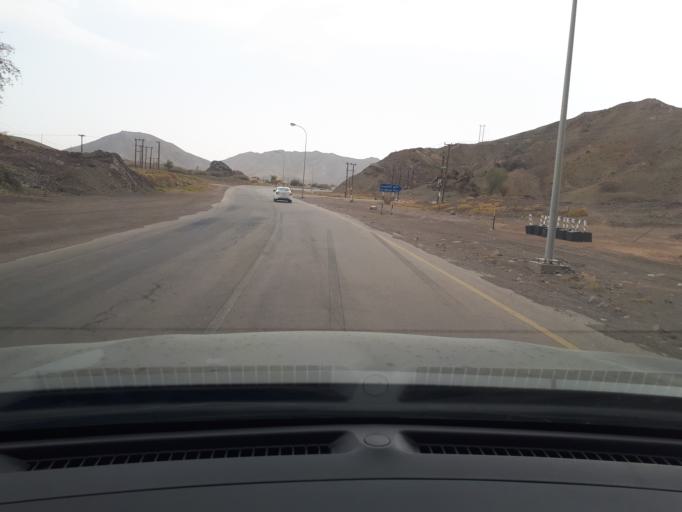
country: OM
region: Ash Sharqiyah
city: Badiyah
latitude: 22.5511
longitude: 59.0011
